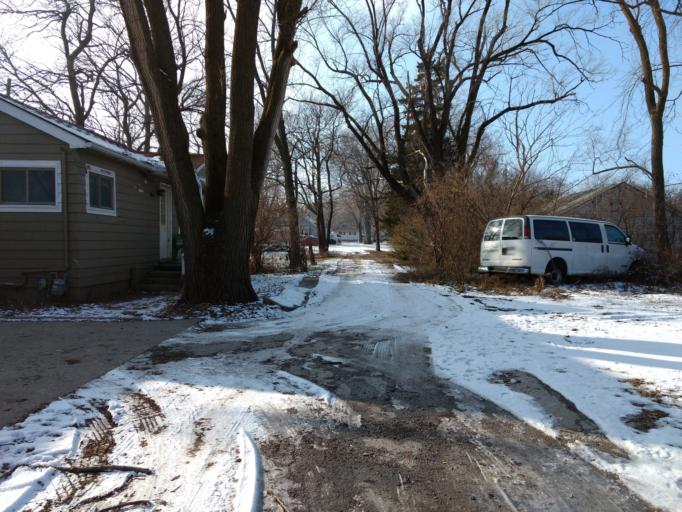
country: US
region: Illinois
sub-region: Champaign County
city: Urbana
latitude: 40.1081
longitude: -88.1916
